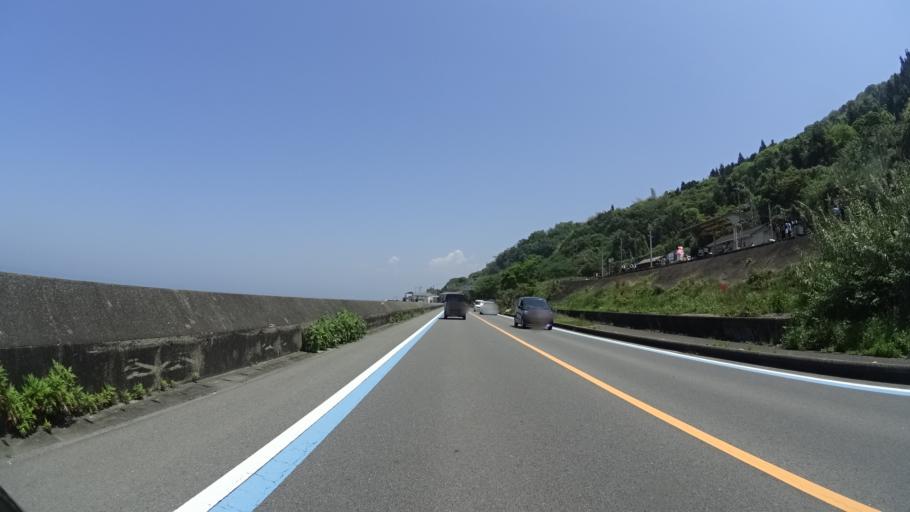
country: JP
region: Ehime
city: Iyo
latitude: 33.6552
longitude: 132.5885
